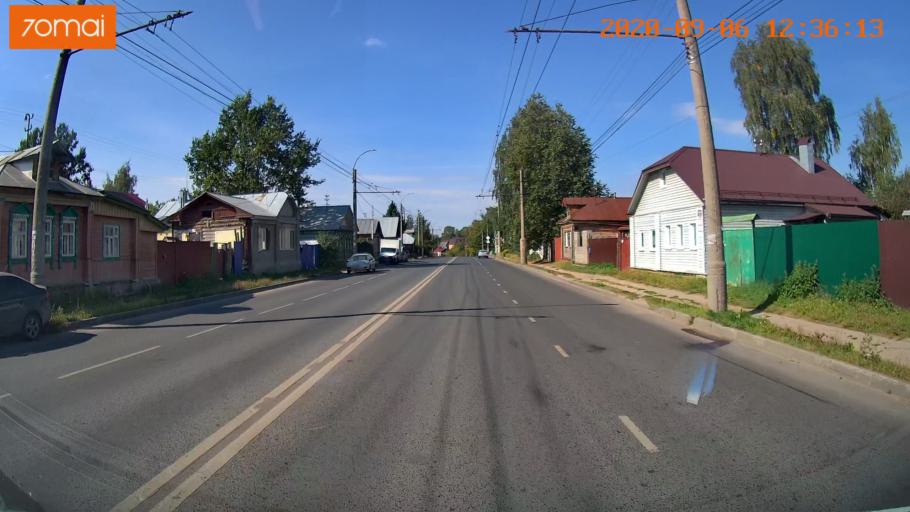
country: RU
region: Ivanovo
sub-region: Gorod Ivanovo
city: Ivanovo
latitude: 57.0221
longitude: 40.9867
